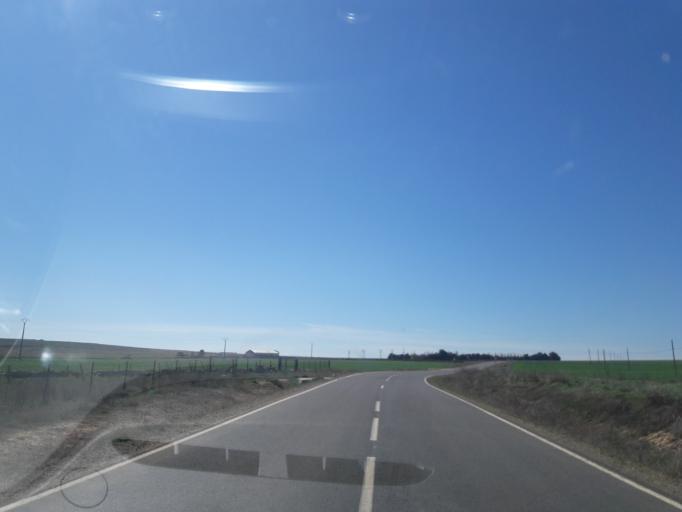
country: ES
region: Castille and Leon
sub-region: Provincia de Salamanca
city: Valdemierque
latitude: 40.8191
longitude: -5.5865
